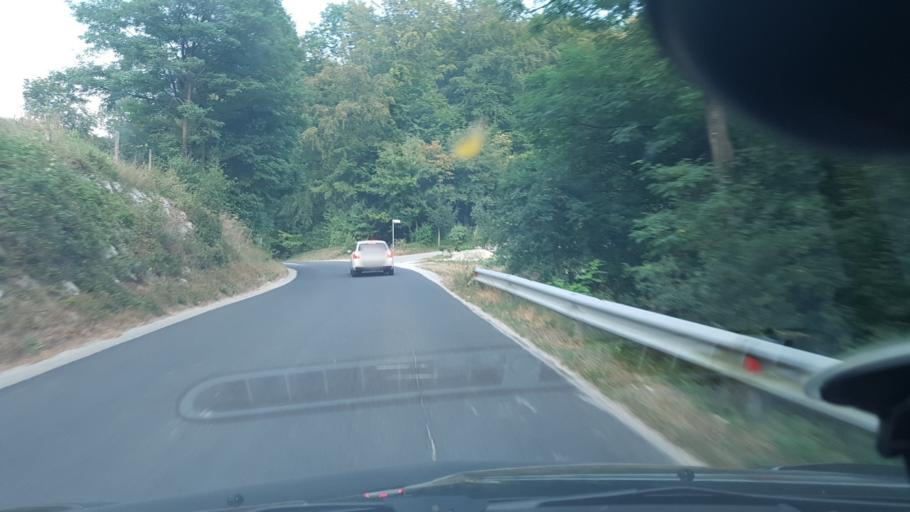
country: SI
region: Kozje
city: Kozje
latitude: 46.1051
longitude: 15.5911
